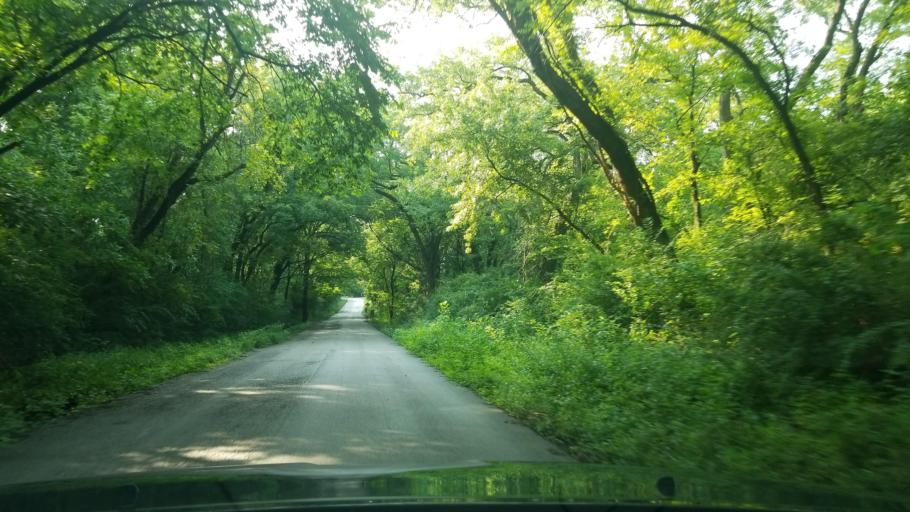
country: US
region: Texas
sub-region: Denton County
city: Cross Roads
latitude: 33.2567
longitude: -97.0612
